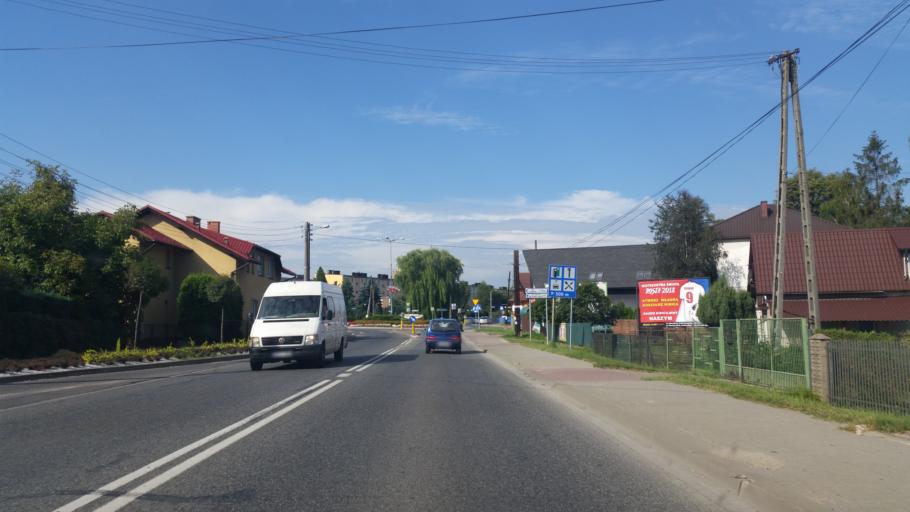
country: PL
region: Lesser Poland Voivodeship
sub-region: Powiat chrzanowski
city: Libiaz
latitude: 50.1072
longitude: 19.3310
